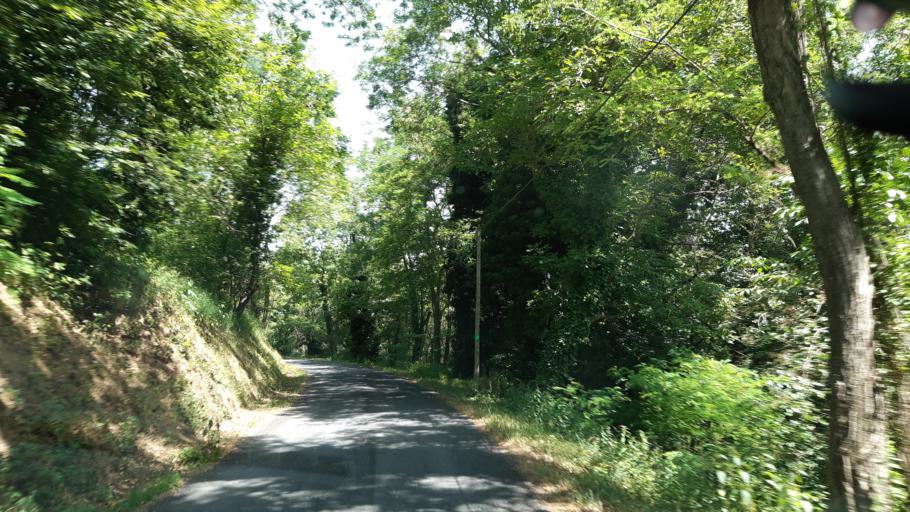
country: FR
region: Languedoc-Roussillon
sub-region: Departement des Pyrenees-Orientales
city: Arles
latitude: 42.5436
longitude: 2.5879
